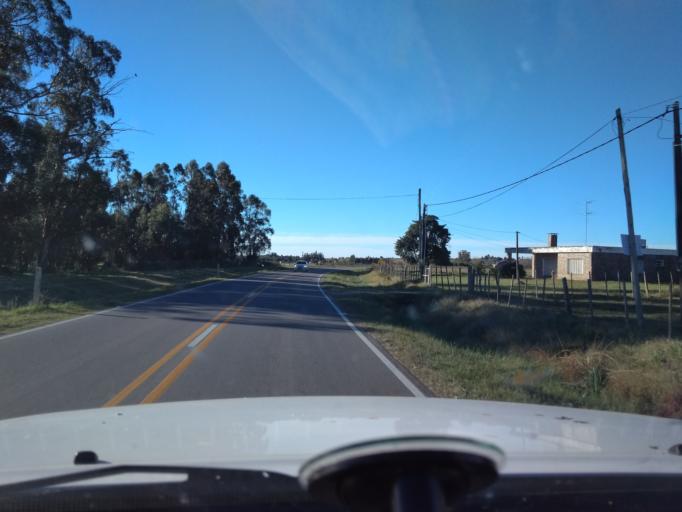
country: UY
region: Canelones
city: Santa Rosa
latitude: -34.5105
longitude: -56.0537
